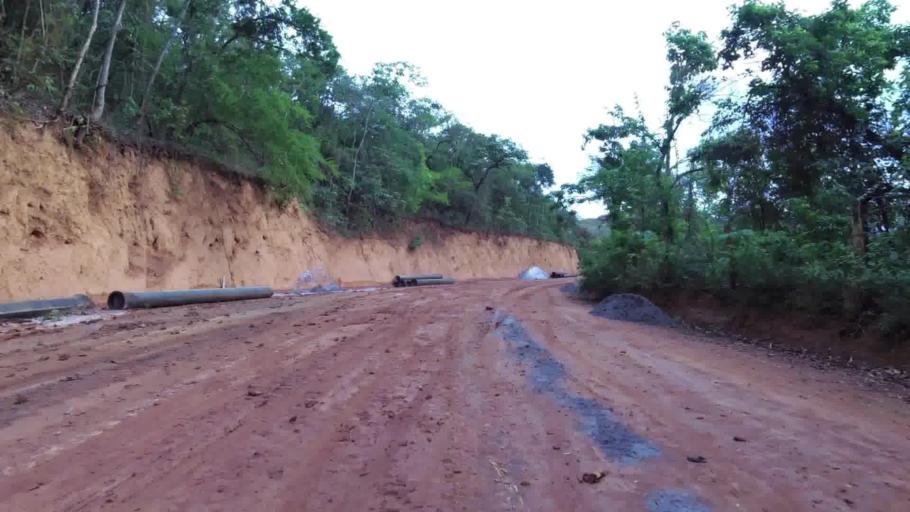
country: BR
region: Espirito Santo
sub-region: Piuma
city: Piuma
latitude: -20.8139
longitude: -40.6736
